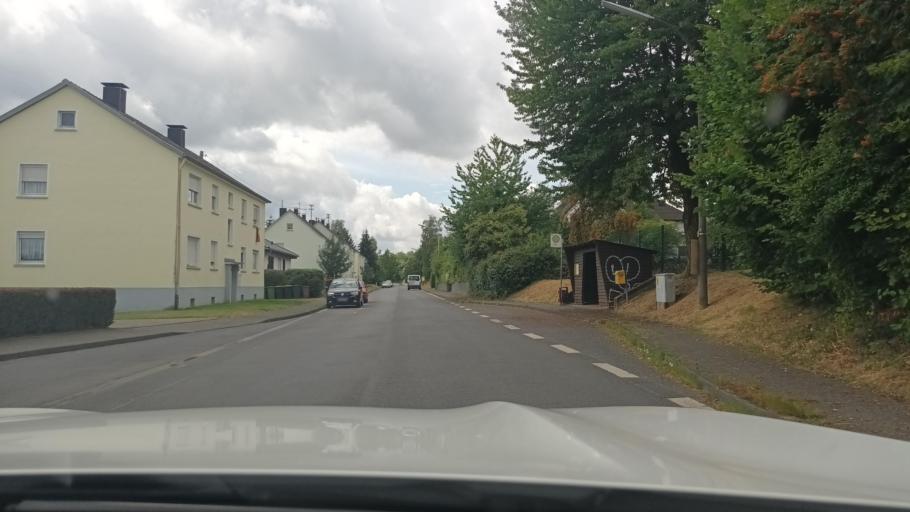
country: DE
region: North Rhine-Westphalia
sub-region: Regierungsbezirk Koln
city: Eitorf
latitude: 50.7515
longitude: 7.4300
